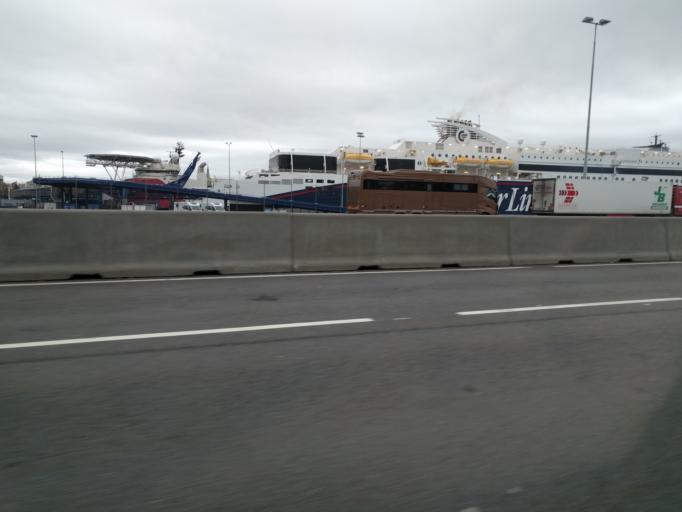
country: NO
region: Vest-Agder
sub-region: Kristiansand
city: Kristiansand
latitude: 58.1436
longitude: 7.9828
